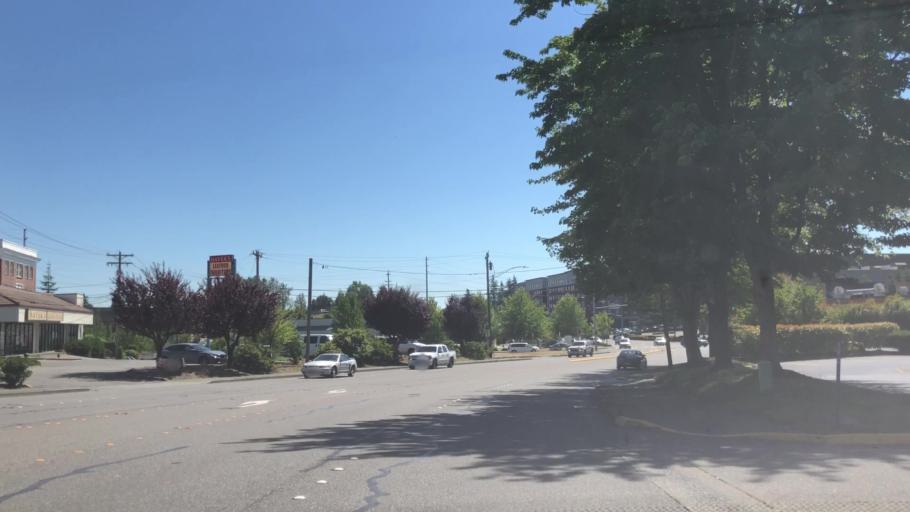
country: US
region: Washington
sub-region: Snohomish County
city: Alderwood Manor
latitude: 47.8232
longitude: -122.2820
